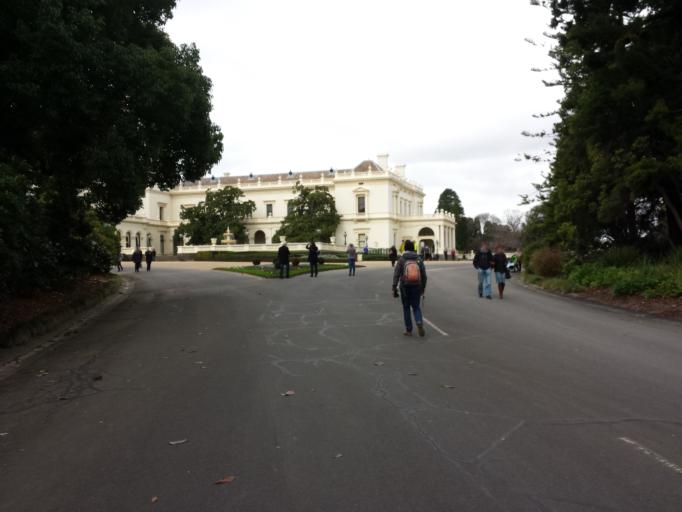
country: AU
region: Victoria
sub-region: Port Phillip
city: South Melbourne
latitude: -37.8278
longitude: 144.9757
